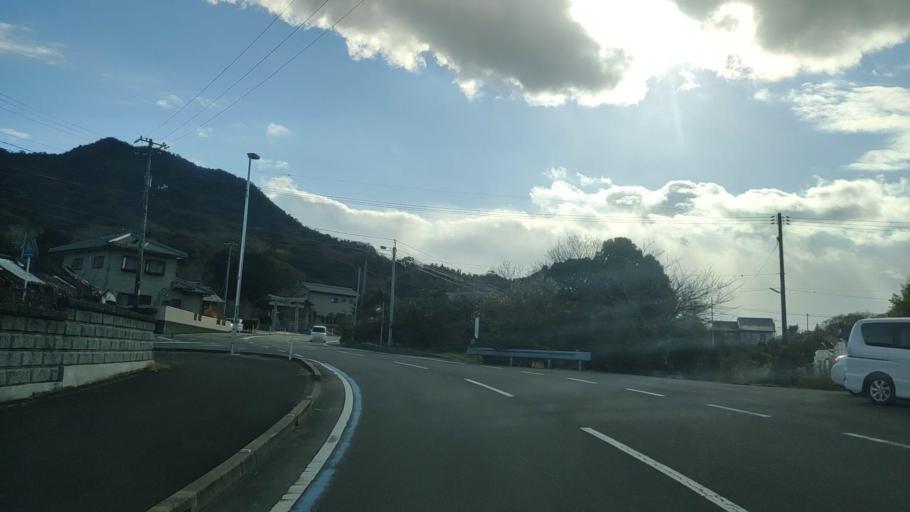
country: JP
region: Hiroshima
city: Innoshima
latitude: 34.2270
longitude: 133.0737
